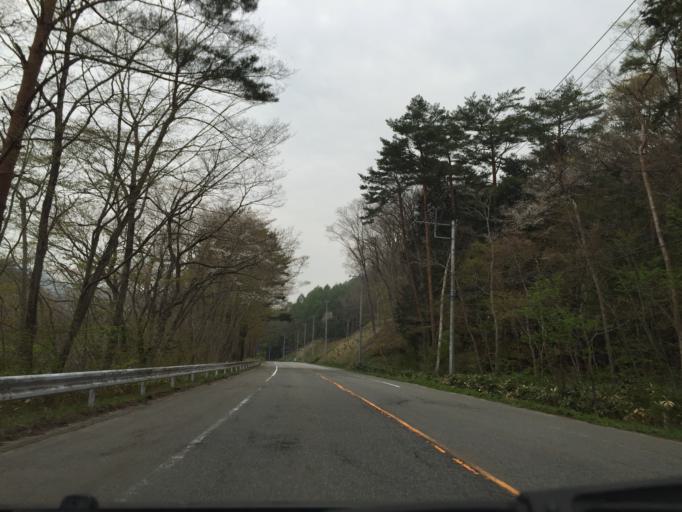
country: JP
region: Tochigi
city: Nikko
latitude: 37.0310
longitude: 139.7275
